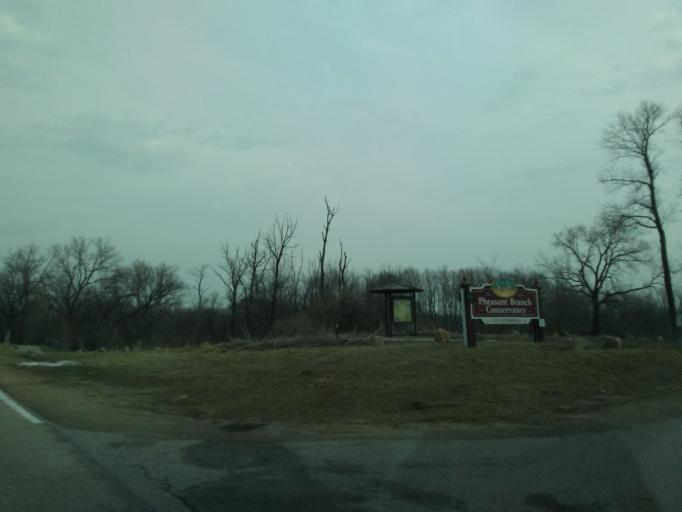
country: US
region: Wisconsin
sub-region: Dane County
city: Middleton
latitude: 43.1144
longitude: -89.4914
